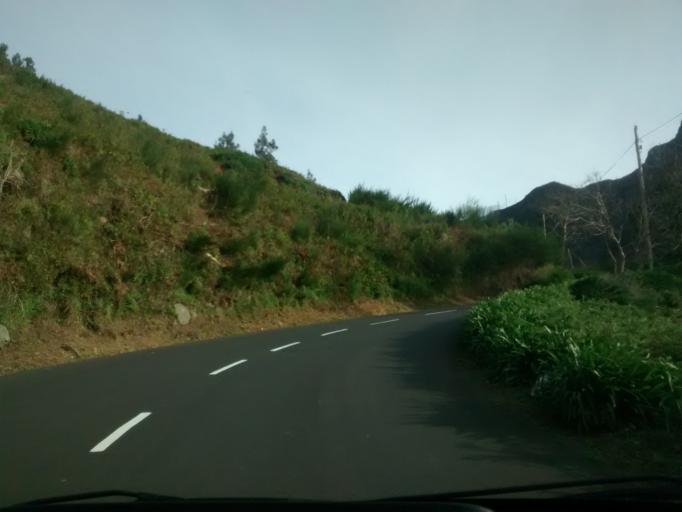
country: PT
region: Madeira
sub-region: Sao Vicente
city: Sao Vicente
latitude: 32.7423
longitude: -17.0252
